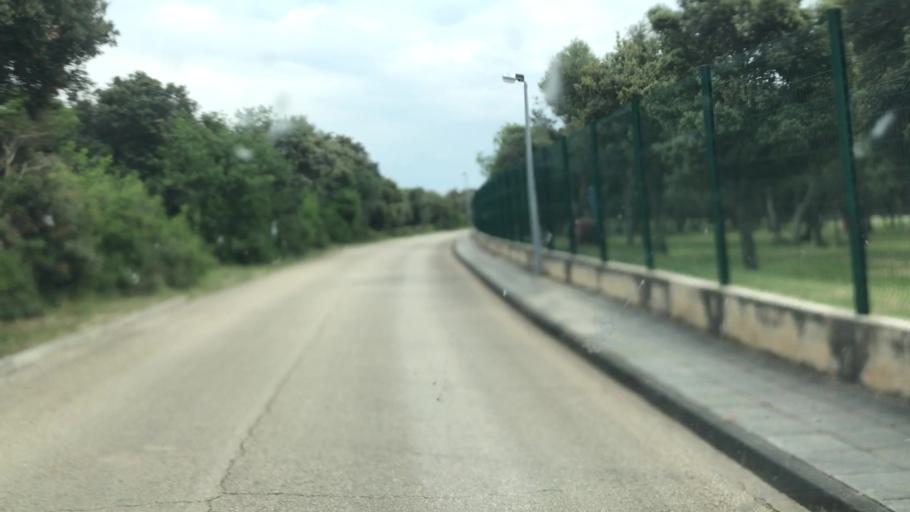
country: HR
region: Licko-Senjska
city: Novalja
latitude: 44.5435
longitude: 14.8833
